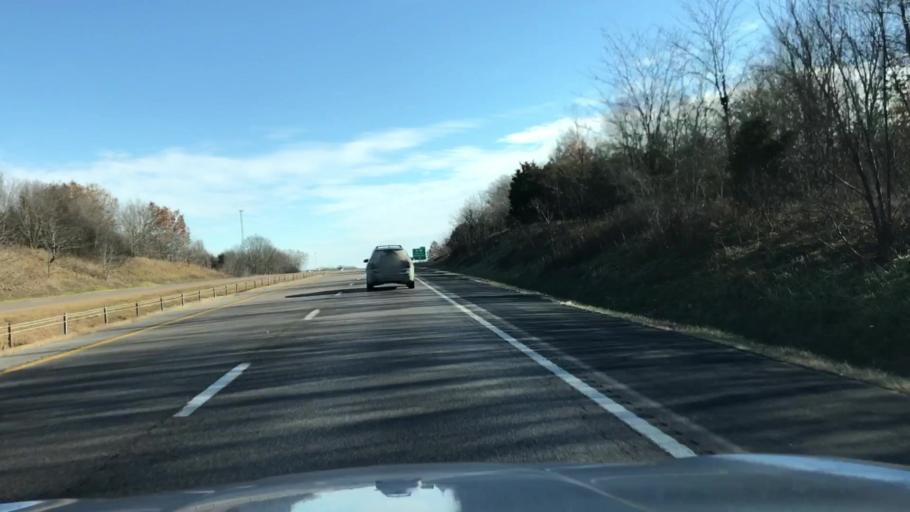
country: US
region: Missouri
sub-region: Cooper County
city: Boonville
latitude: 38.9394
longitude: -92.6055
